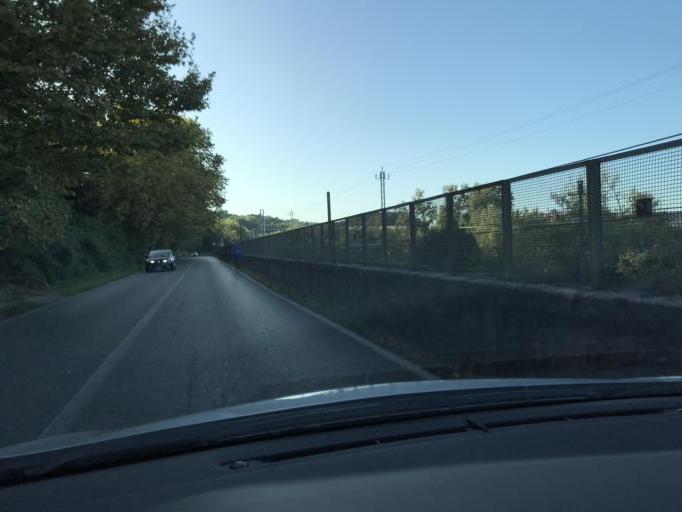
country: IT
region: Latium
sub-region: Provincia di Viterbo
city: Orte Scalo
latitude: 42.4459
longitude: 12.3964
